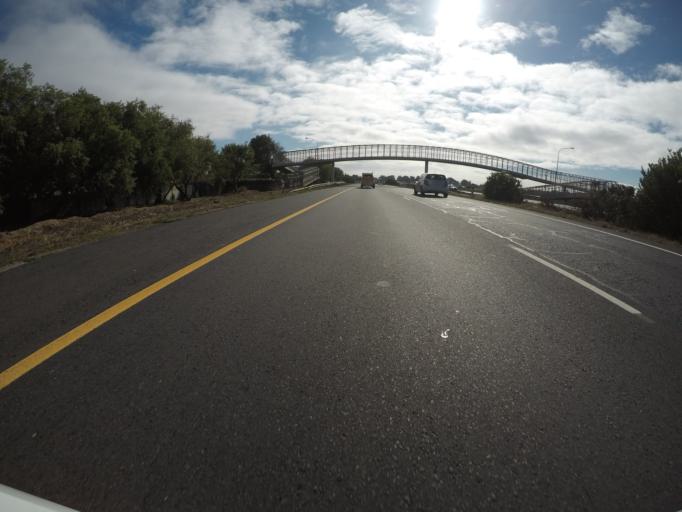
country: ZA
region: Western Cape
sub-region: City of Cape Town
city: Kraaifontein
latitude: -33.8492
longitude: 18.7088
